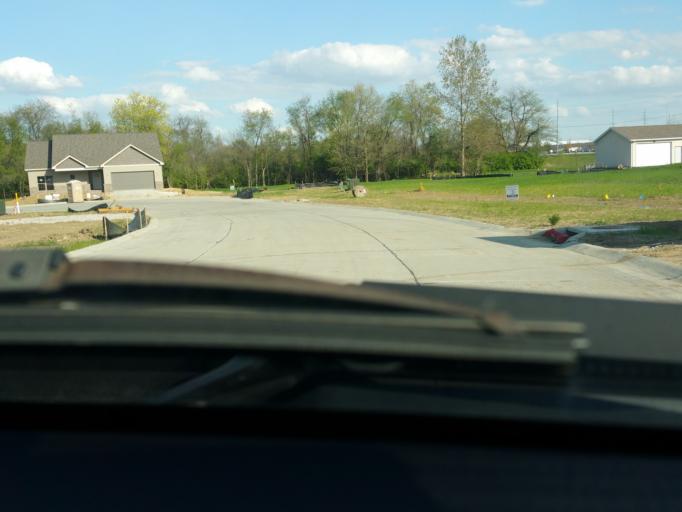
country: US
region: Illinois
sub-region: Madison County
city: Edwardsville
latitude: 38.7887
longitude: -89.9636
